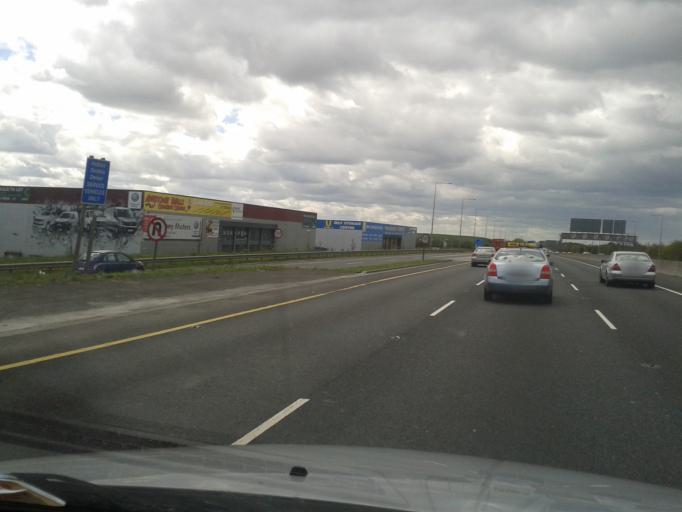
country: IE
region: Leinster
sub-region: Dublin City
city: Finglas
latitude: 53.4029
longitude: -6.3150
